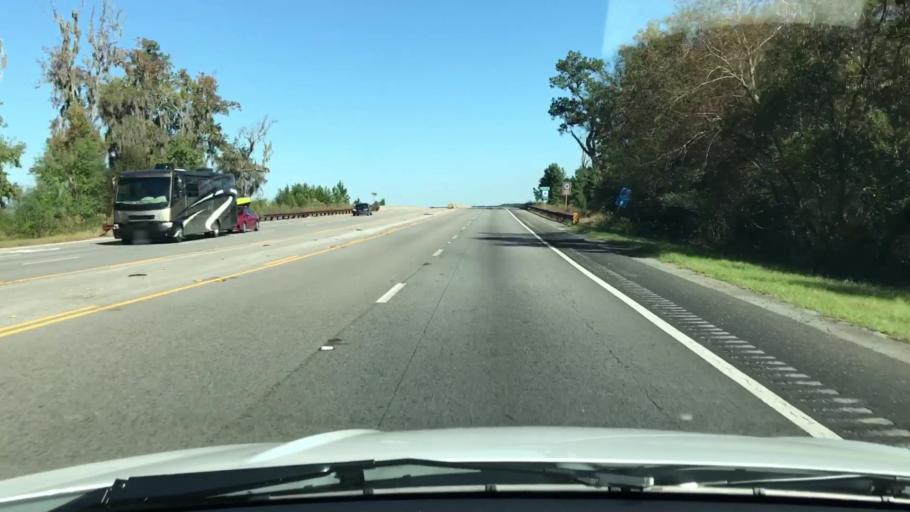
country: US
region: South Carolina
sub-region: Hampton County
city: Yemassee
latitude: 32.6518
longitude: -80.6848
